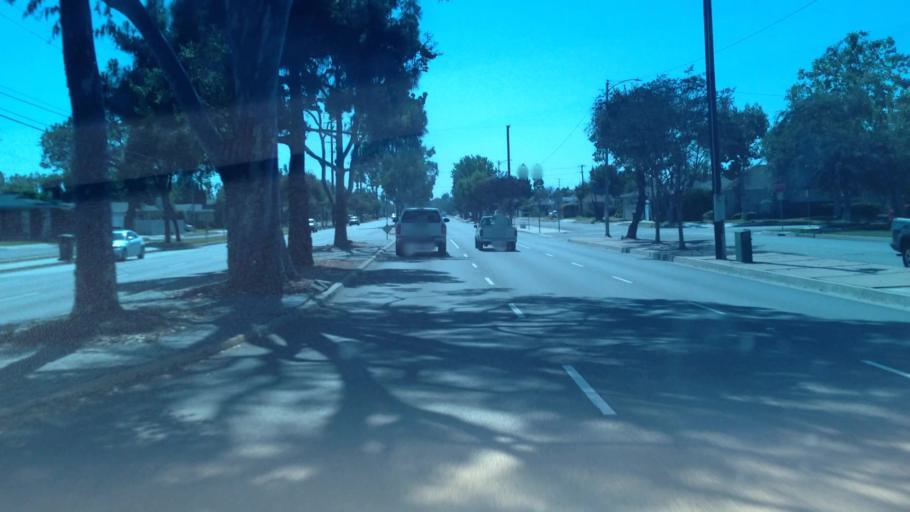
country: US
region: California
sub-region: Orange County
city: Los Alamitos
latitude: 33.8105
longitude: -118.1011
